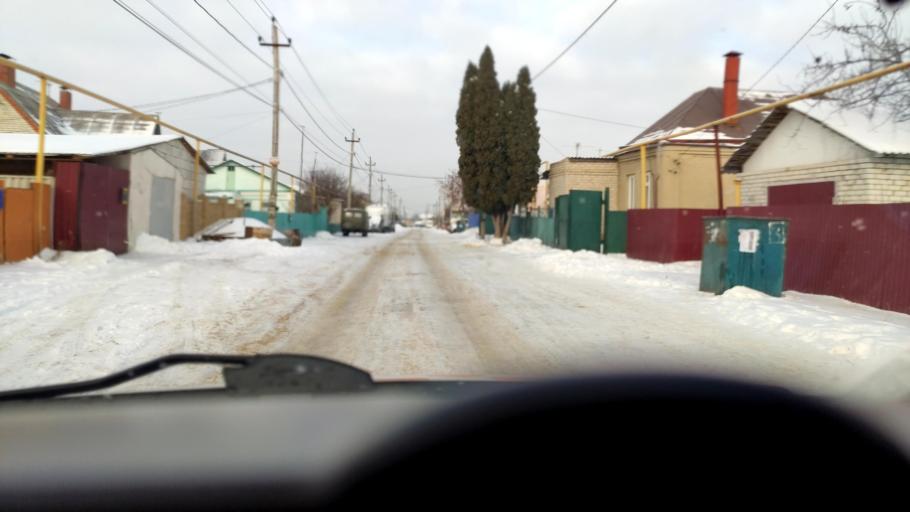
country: RU
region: Voronezj
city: Podgornoye
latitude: 51.7265
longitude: 39.1557
